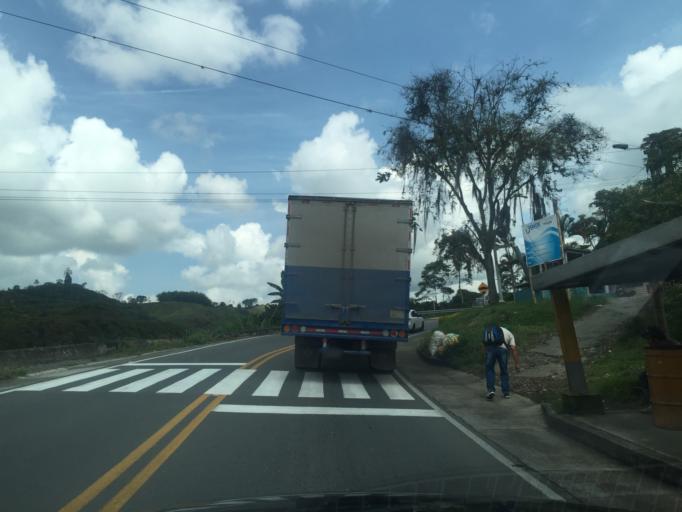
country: CO
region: Caldas
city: Chinchina
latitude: 4.9984
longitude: -75.5725
